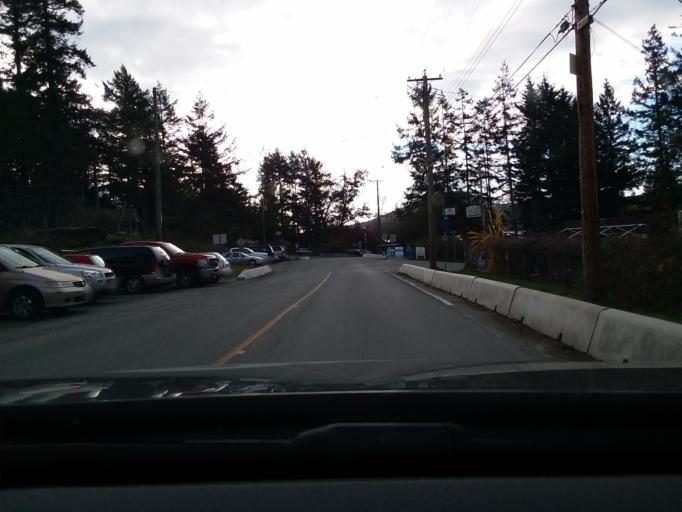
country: CA
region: British Columbia
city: North Saanich
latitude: 48.8790
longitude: -123.3183
